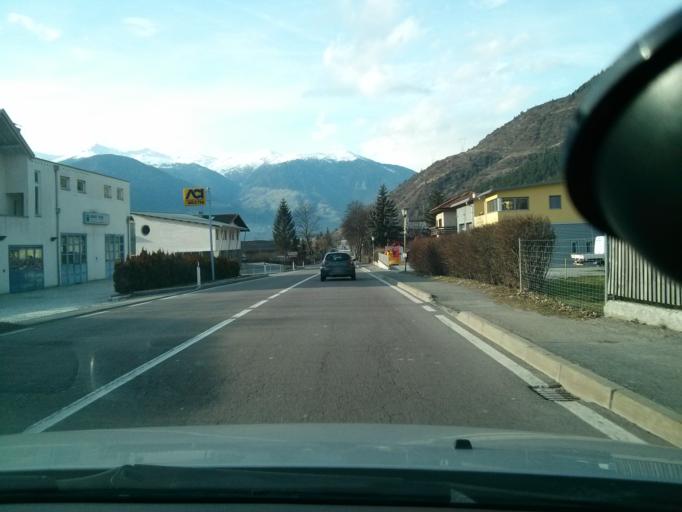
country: IT
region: Trentino-Alto Adige
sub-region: Bolzano
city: Lasa
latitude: 46.6293
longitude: 10.6474
